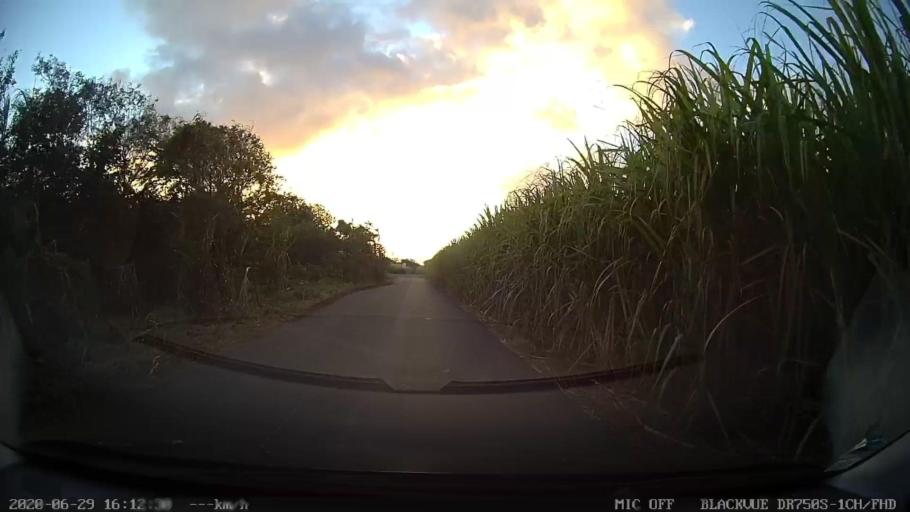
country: RE
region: Reunion
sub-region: Reunion
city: Bras-Panon
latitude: -20.9908
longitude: 55.6917
